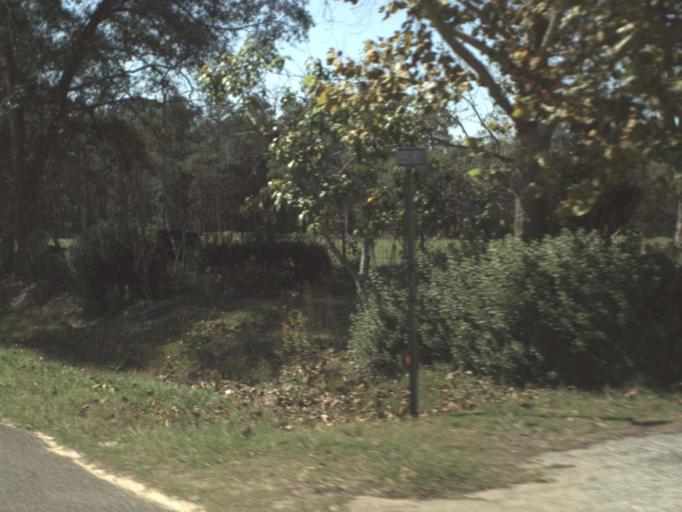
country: US
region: Alabama
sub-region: Geneva County
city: Samson
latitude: 30.9820
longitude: -86.1342
